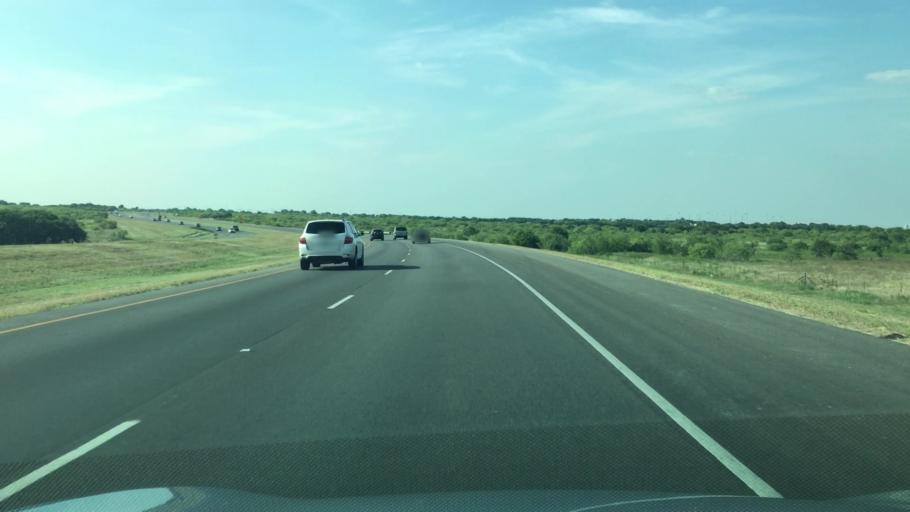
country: US
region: Texas
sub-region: Hays County
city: Kyle
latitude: 30.0357
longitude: -97.8721
